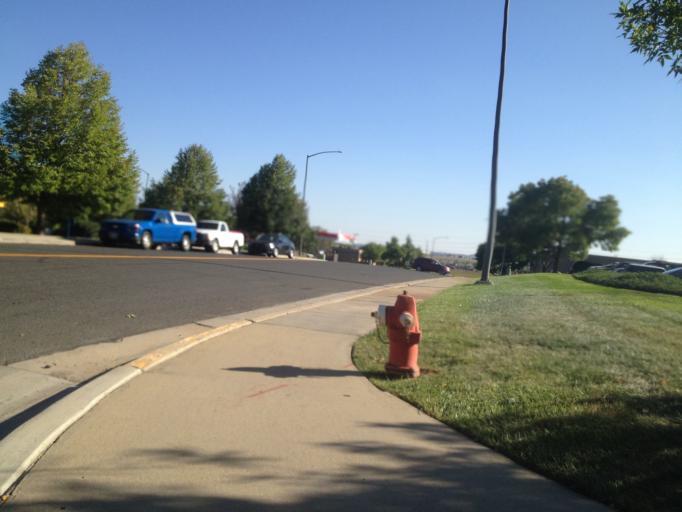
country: US
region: Colorado
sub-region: Boulder County
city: Louisville
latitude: 39.9888
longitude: -105.1233
